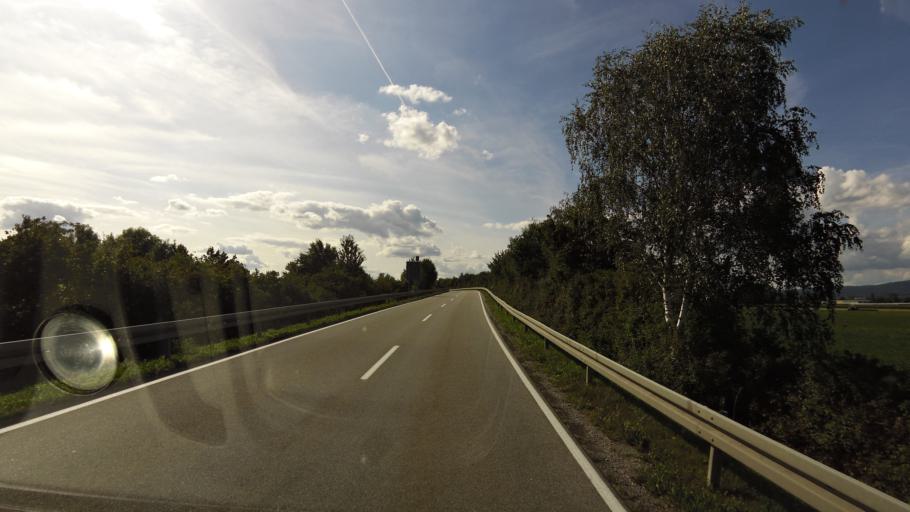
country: DE
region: Bavaria
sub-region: Lower Bavaria
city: Kirchroth
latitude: 48.9247
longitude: 12.5642
